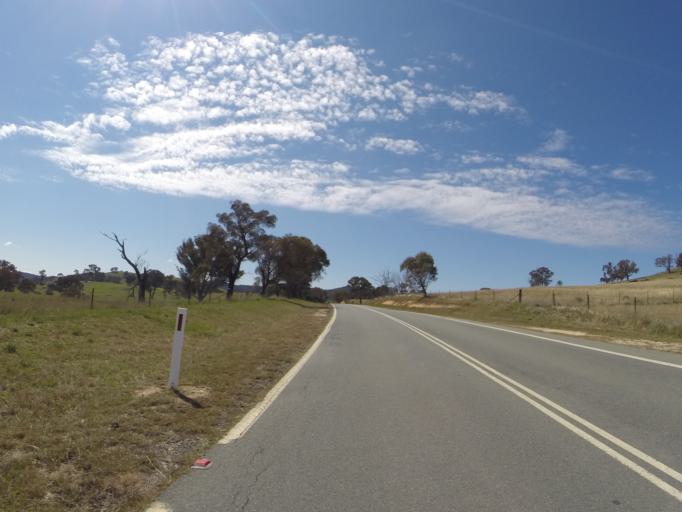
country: AU
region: Australian Capital Territory
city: Macarthur
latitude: -35.4145
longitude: 148.9675
